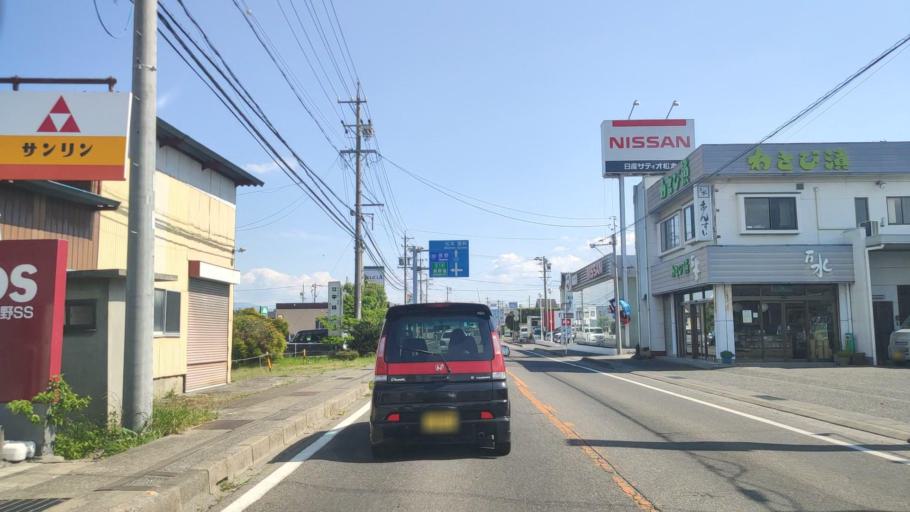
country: JP
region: Nagano
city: Hotaka
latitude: 36.3253
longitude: 137.8931
